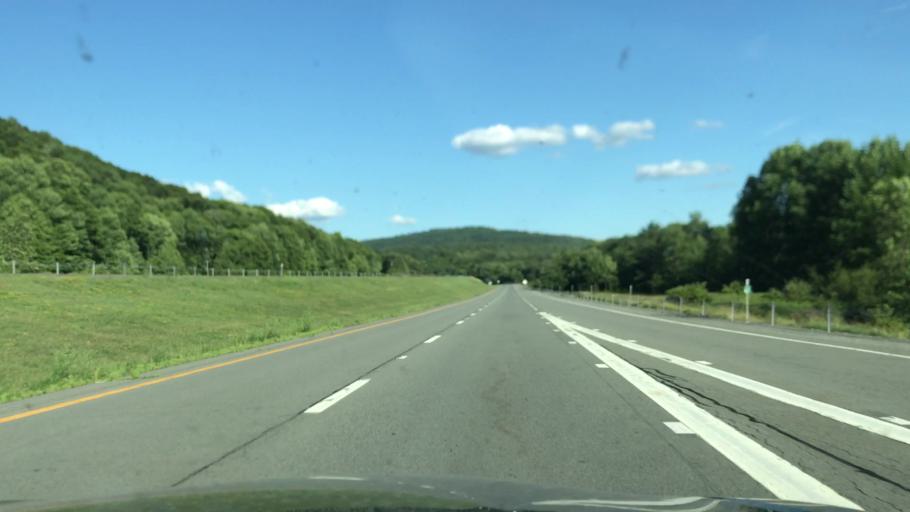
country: US
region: New York
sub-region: Sullivan County
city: Livingston Manor
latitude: 41.9561
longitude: -74.9870
